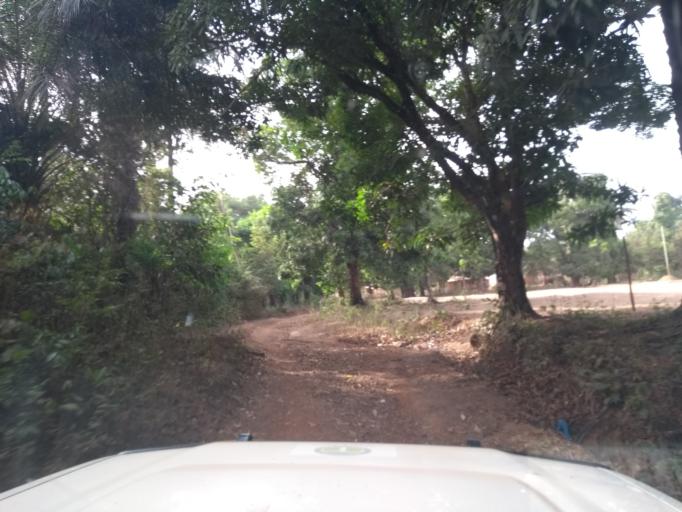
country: GN
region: Kindia
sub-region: Prefecture de Dubreka
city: Dubreka
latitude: 9.8329
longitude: -13.5570
